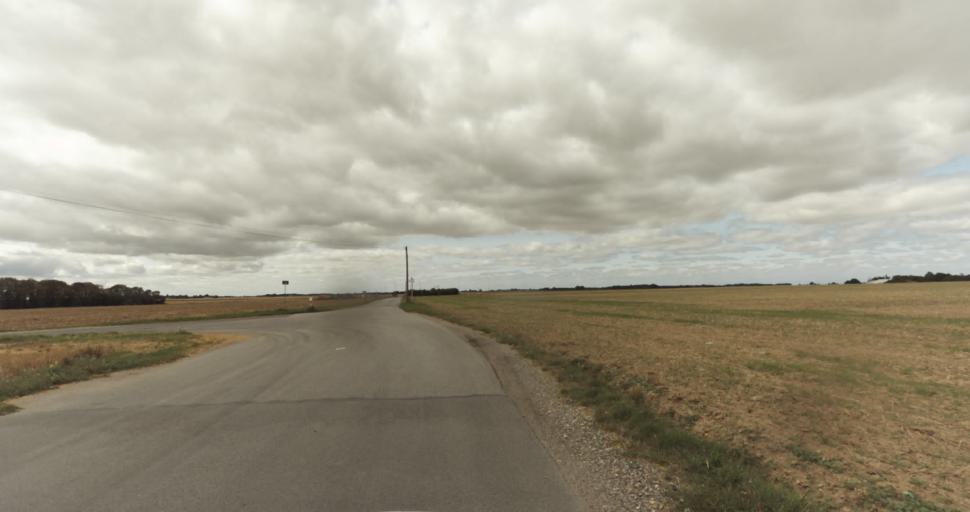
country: FR
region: Haute-Normandie
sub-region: Departement de l'Eure
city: Marcilly-sur-Eure
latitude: 48.9104
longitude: 1.2618
